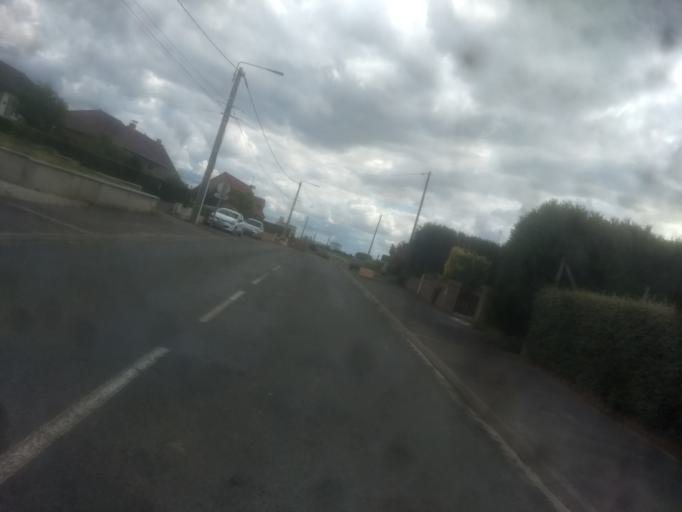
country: FR
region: Nord-Pas-de-Calais
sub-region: Departement du Pas-de-Calais
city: Agny
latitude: 50.2259
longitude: 2.7437
